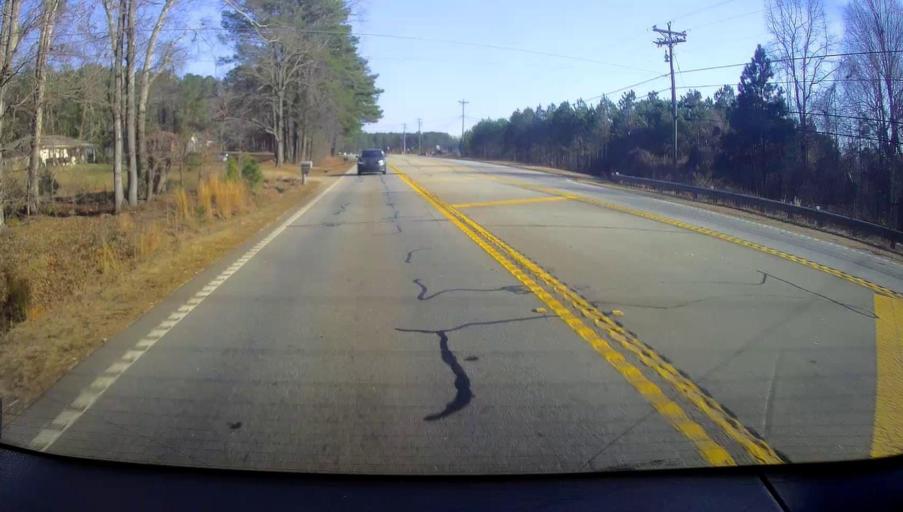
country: US
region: Georgia
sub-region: Henry County
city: Locust Grove
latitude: 33.3359
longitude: -84.0917
